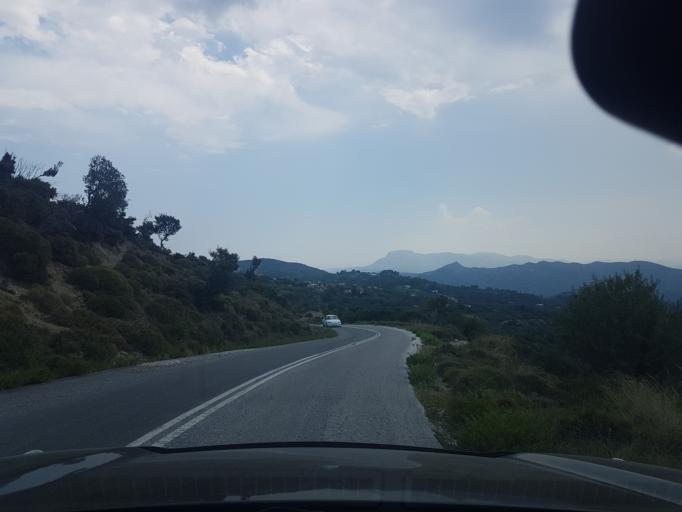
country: GR
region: Central Greece
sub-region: Nomos Evvoias
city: Kymi
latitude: 38.6433
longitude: 24.0620
